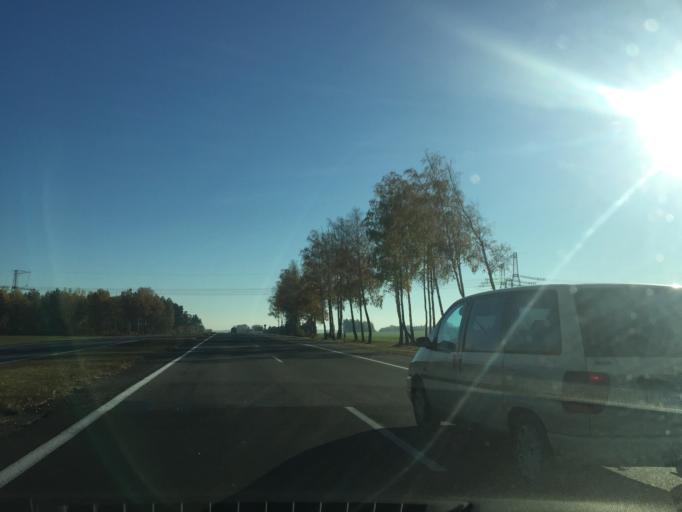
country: BY
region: Minsk
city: Smilavichy
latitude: 53.7639
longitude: 28.1089
